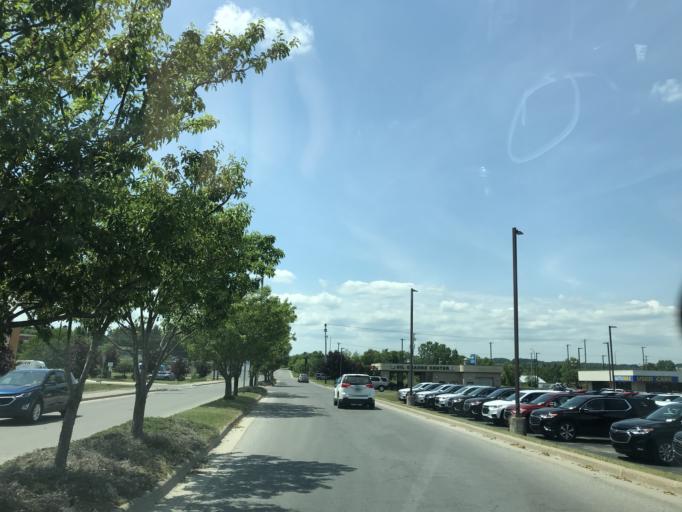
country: US
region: Michigan
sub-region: Grand Traverse County
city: Traverse City
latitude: 44.7248
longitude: -85.6440
